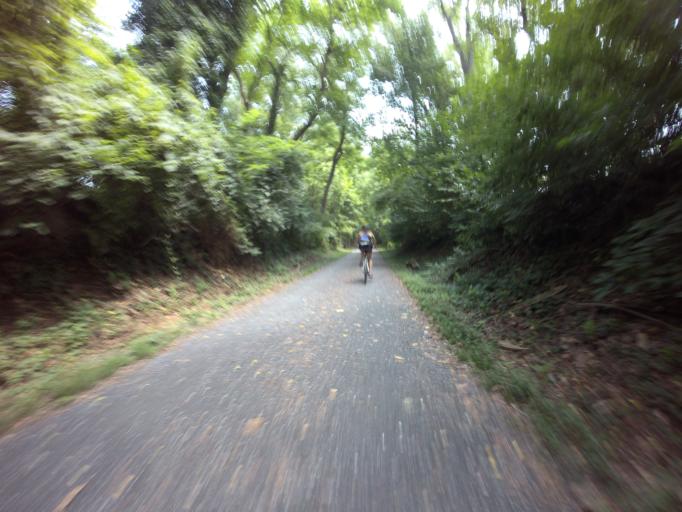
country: US
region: Maryland
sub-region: Montgomery County
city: Chevy Chase
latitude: 38.9954
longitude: -77.0748
